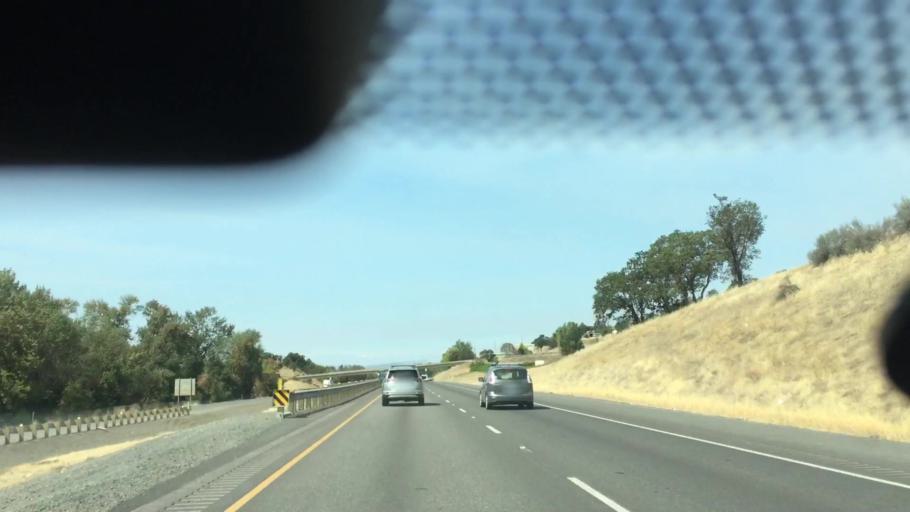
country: US
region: Oregon
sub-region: Jackson County
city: Talent
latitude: 42.2506
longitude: -122.7796
